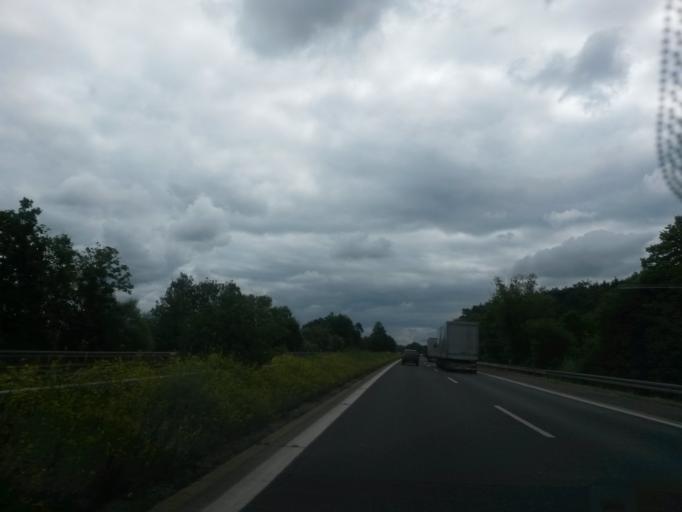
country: DE
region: Bavaria
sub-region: Regierungsbezirk Mittelfranken
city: Burghaslach
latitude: 49.7621
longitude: 10.5514
